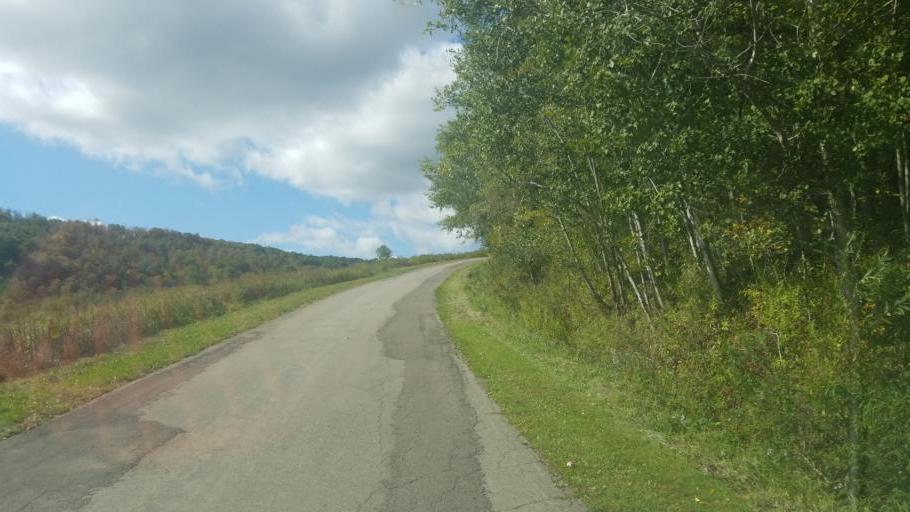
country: US
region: New York
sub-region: Cattaraugus County
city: Franklinville
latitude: 42.2340
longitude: -78.4029
